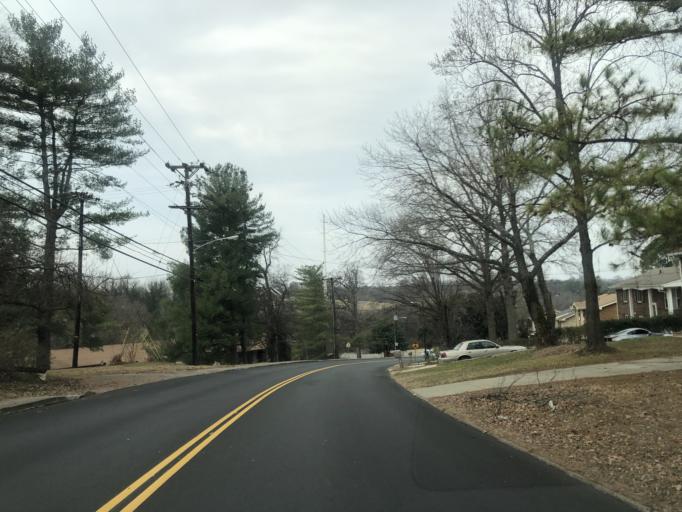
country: US
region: Tennessee
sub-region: Davidson County
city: Oak Hill
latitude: 36.0877
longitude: -86.7152
